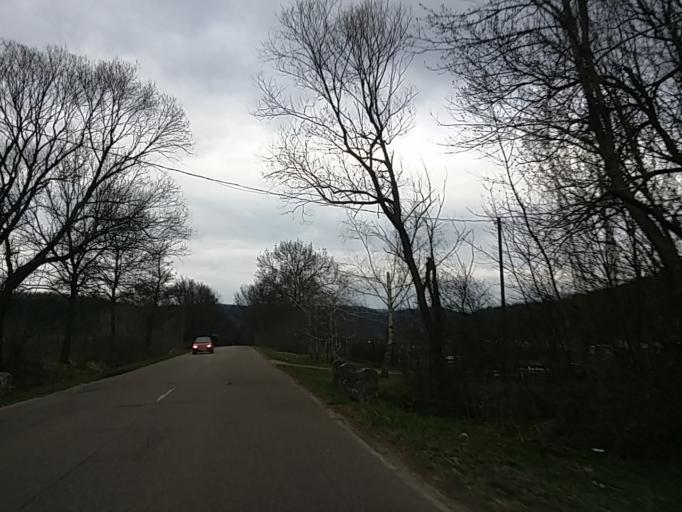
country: HU
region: Heves
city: Sirok
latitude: 47.9090
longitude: 20.1781
